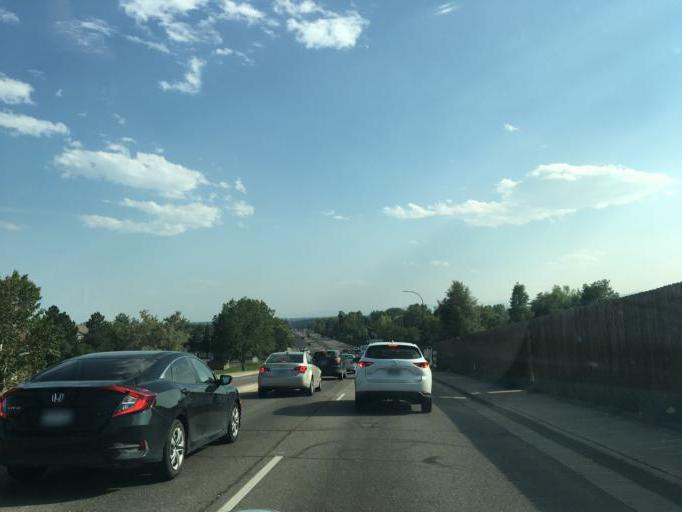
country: US
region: Colorado
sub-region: Adams County
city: Westminster
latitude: 39.8513
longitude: -105.0530
